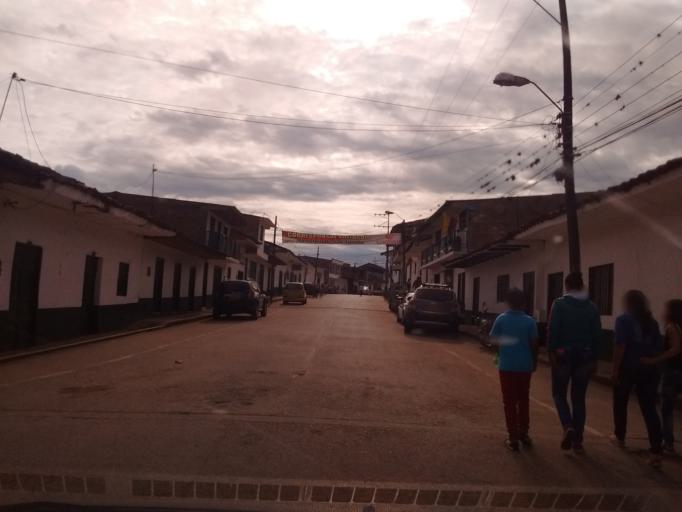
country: CO
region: Huila
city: San Agustin
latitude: 1.8795
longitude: -76.2681
